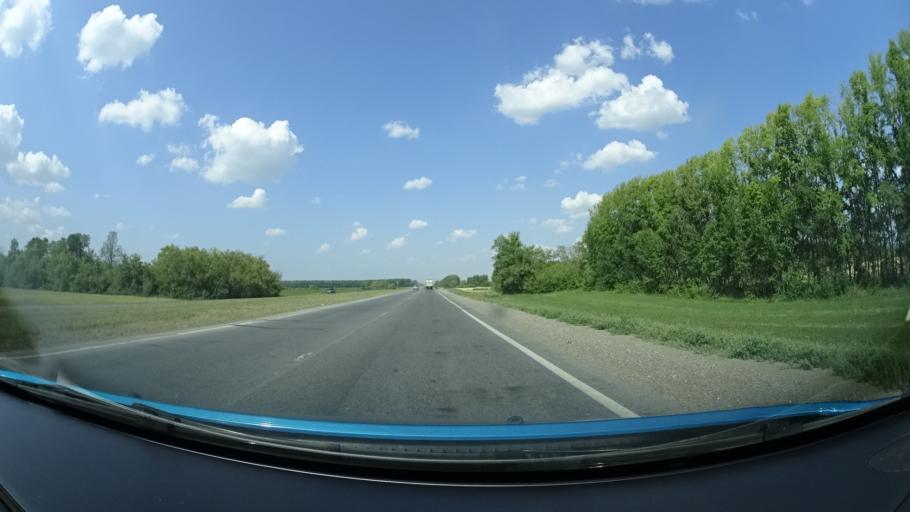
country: RU
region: Bashkortostan
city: Chishmy
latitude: 54.6580
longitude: 55.4694
